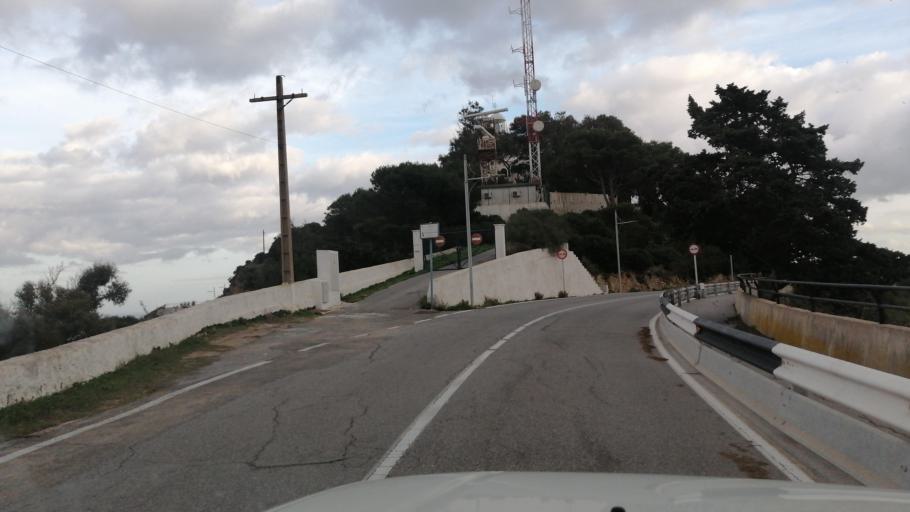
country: ES
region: Ceuta
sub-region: Ceuta
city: Ceuta
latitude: 35.8991
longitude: -5.2824
